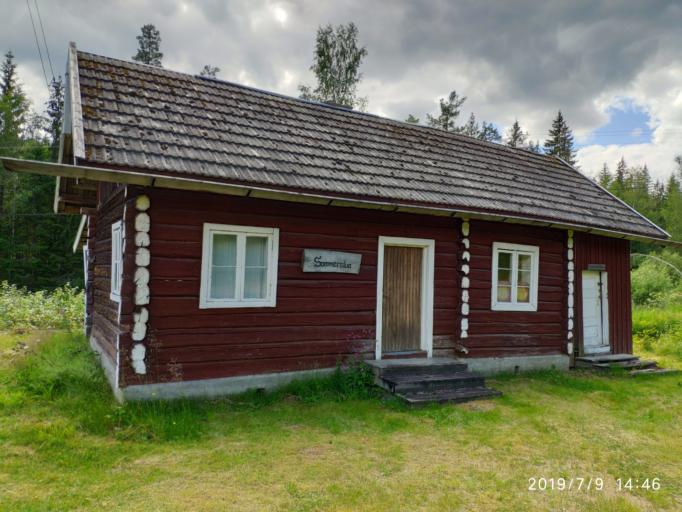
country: NO
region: Buskerud
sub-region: Flesberg
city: Lampeland
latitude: 59.8666
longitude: 9.5584
